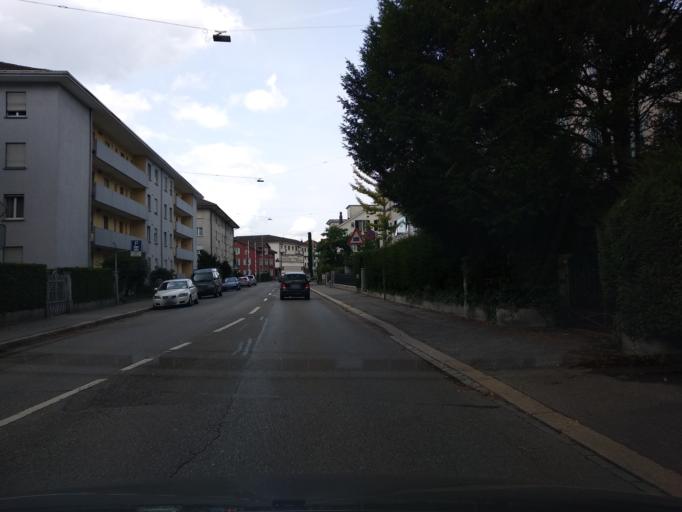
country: CH
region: Zurich
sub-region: Bezirk Winterthur
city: Winterthur
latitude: 47.5060
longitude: 8.7237
